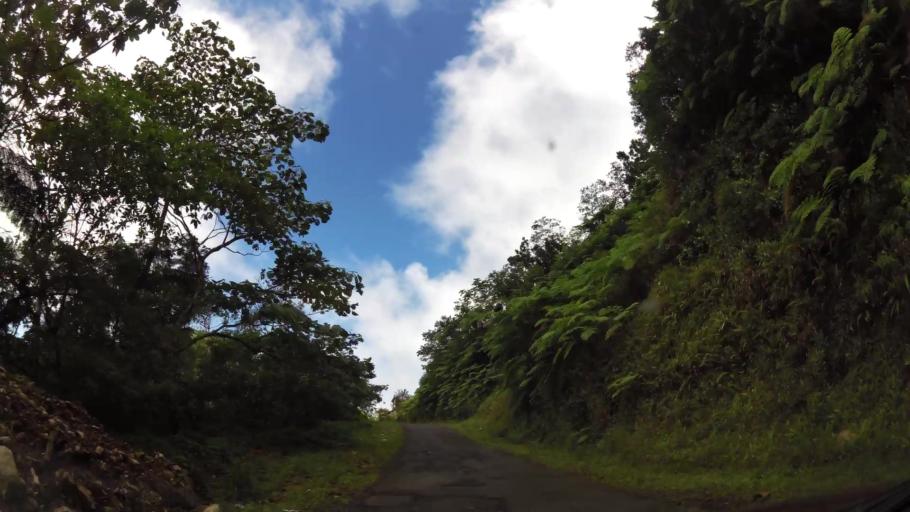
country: DM
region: Saint John
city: Portsmouth
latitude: 15.6208
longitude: -61.4359
